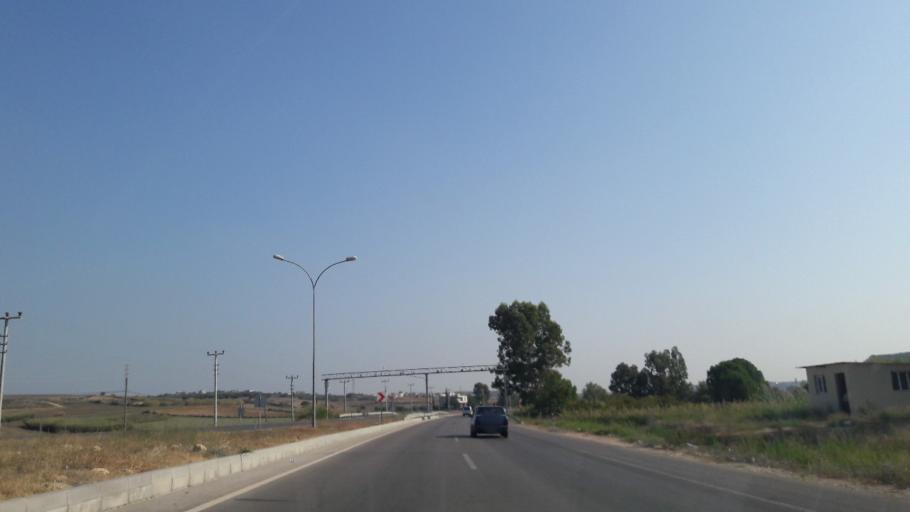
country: TR
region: Adana
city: Yuregir
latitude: 37.0625
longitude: 35.4454
